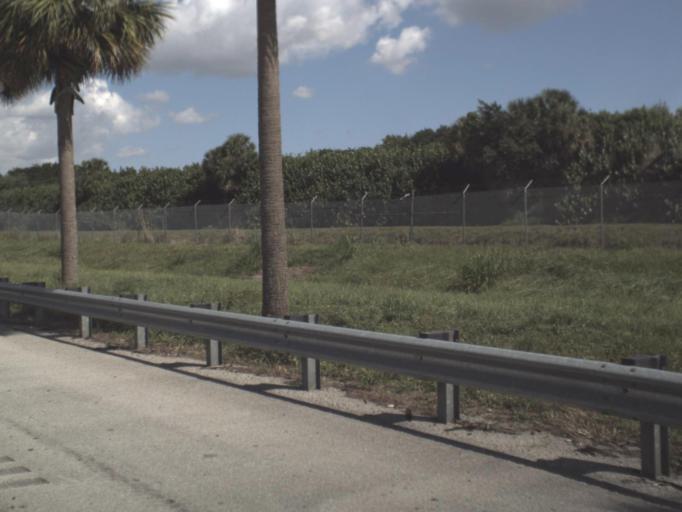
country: US
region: Florida
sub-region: Palm Beach County
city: Villages of Oriole
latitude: 26.4979
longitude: -80.1724
